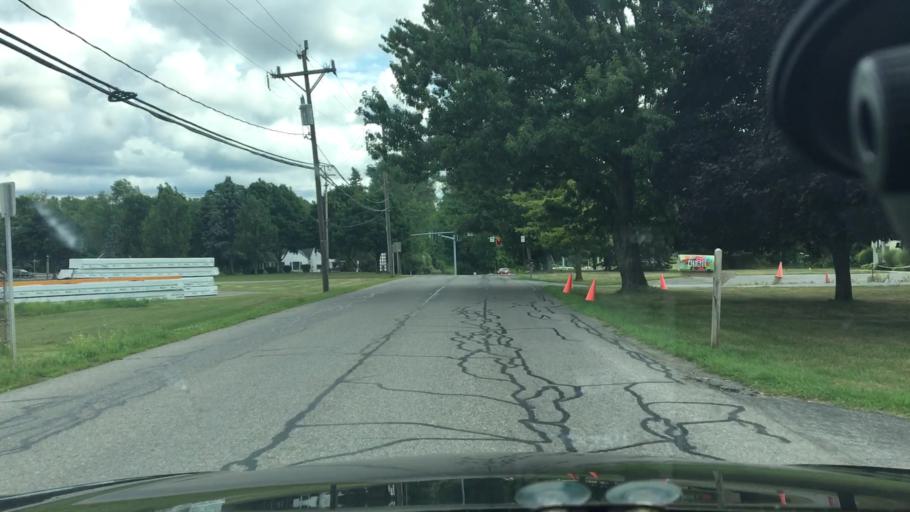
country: US
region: New York
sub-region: Erie County
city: Orchard Park
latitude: 42.7646
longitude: -78.7613
